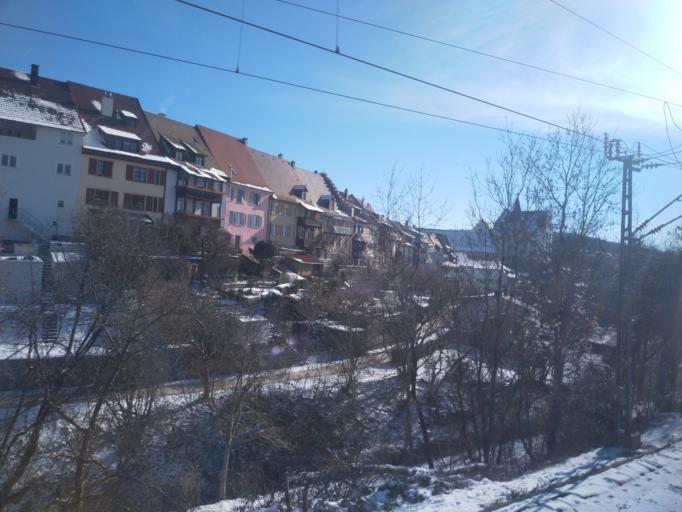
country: DE
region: Baden-Wuerttemberg
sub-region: Freiburg Region
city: Engen
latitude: 47.8516
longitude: 8.7686
